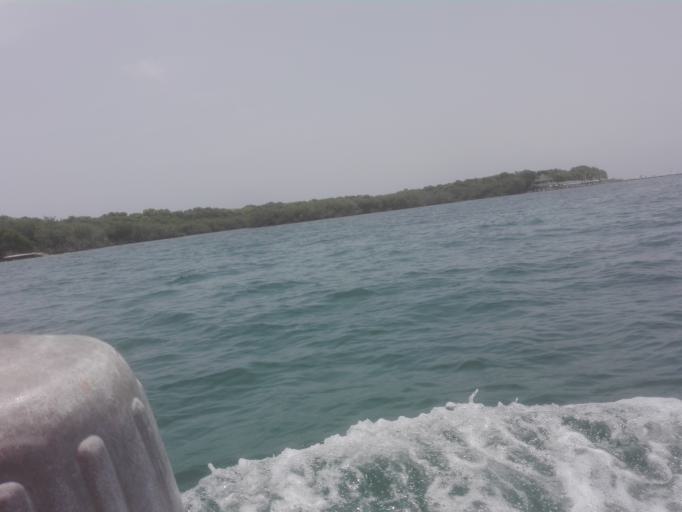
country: CO
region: Bolivar
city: Turbana
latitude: 10.1759
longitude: -75.7298
